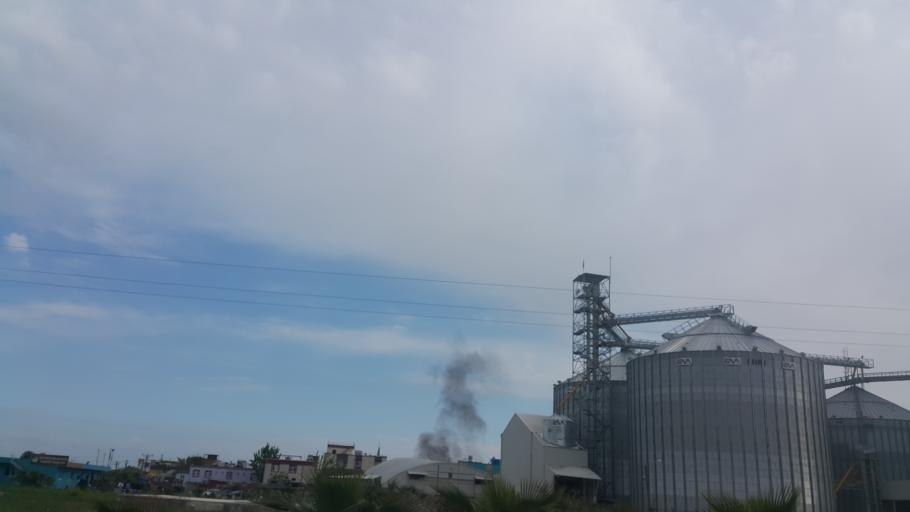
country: TR
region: Mersin
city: Yenice
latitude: 36.9881
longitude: 35.1432
